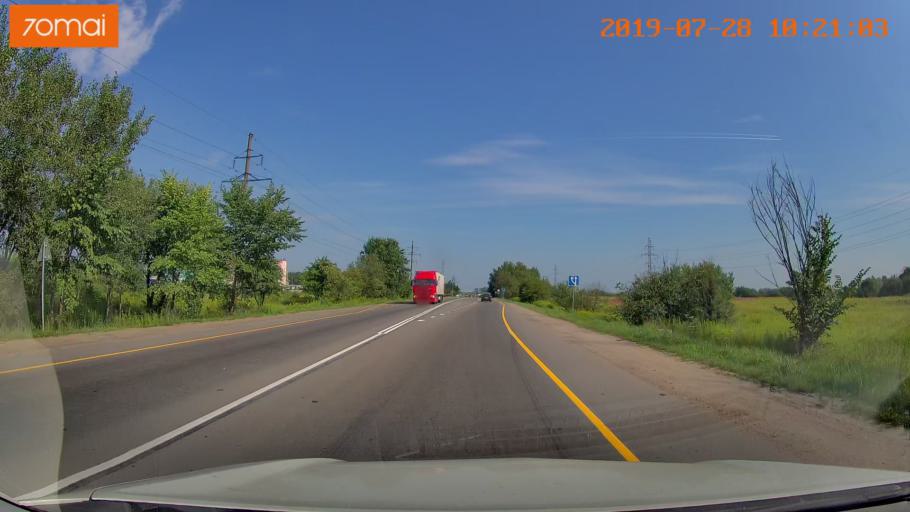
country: RU
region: Kaliningrad
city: Maloye Isakovo
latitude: 54.7537
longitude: 20.5655
